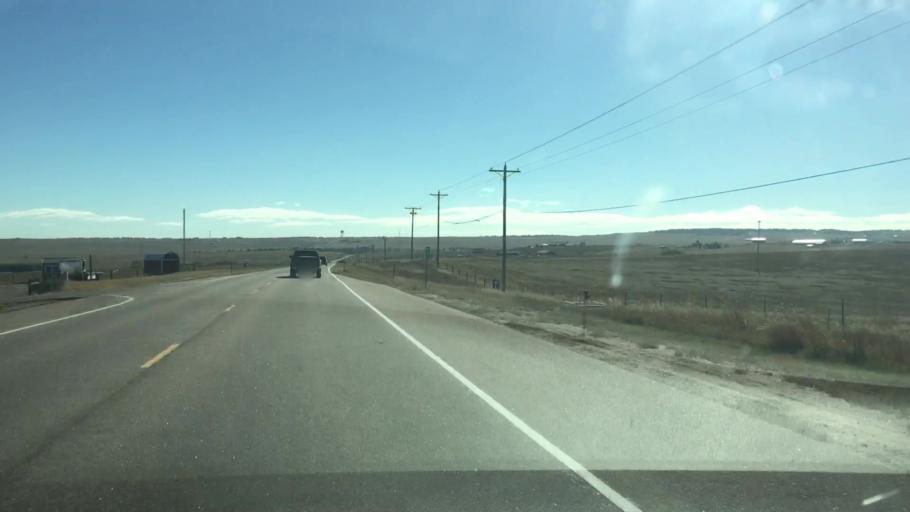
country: US
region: Colorado
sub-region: Elbert County
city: Kiowa
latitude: 39.3534
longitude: -104.5026
